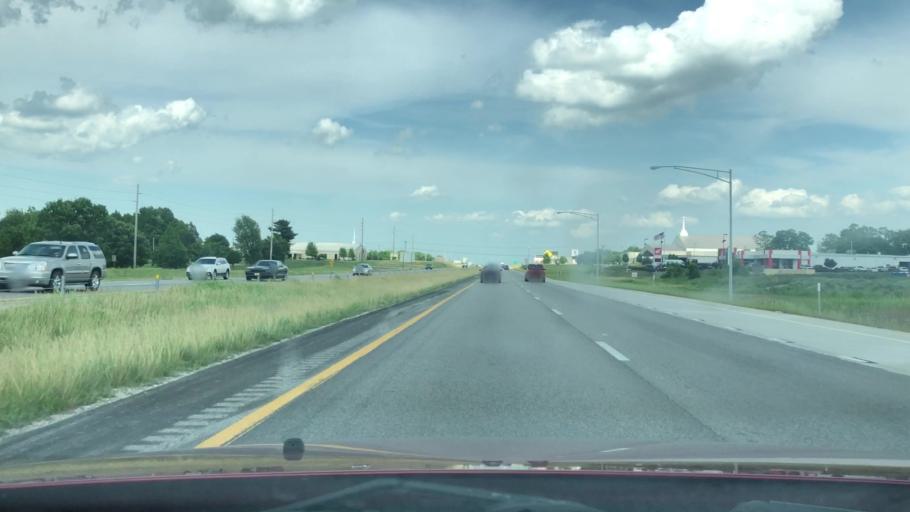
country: US
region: Missouri
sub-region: Greene County
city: Springfield
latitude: 37.2502
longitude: -93.2557
